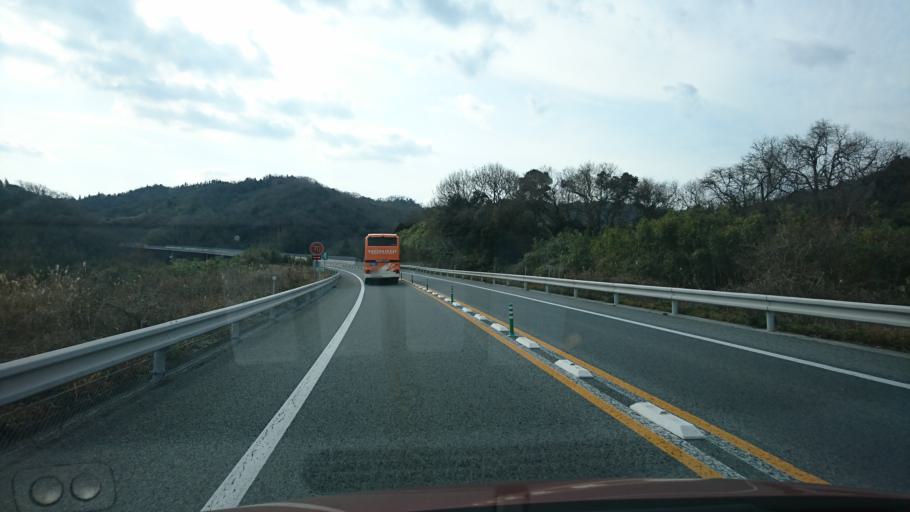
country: JP
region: Hiroshima
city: Innoshima
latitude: 34.1691
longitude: 133.0644
